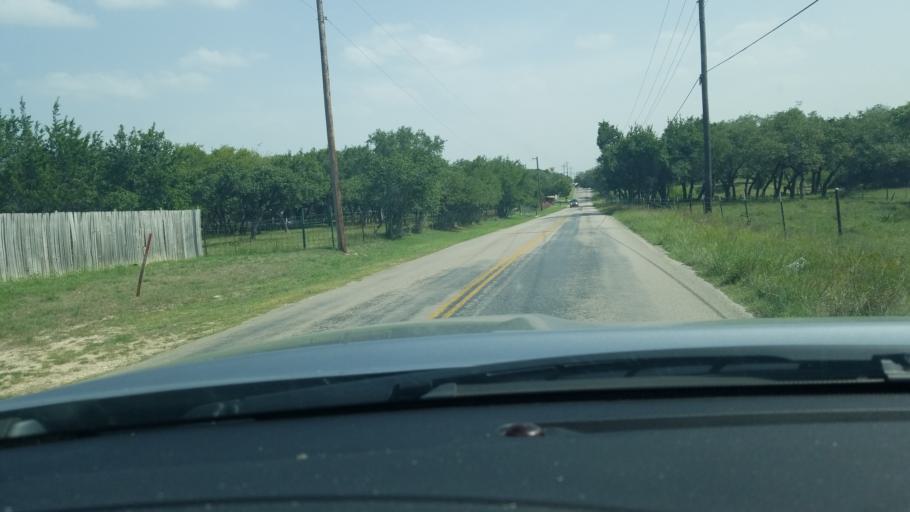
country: US
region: Texas
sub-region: Comal County
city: Bulverde
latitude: 29.7753
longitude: -98.4588
